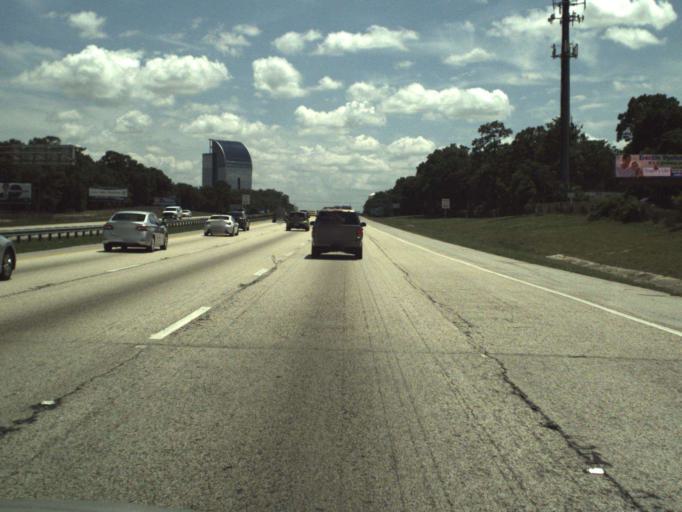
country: US
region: Florida
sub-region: Seminole County
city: Altamonte Springs
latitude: 28.6818
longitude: -81.3888
